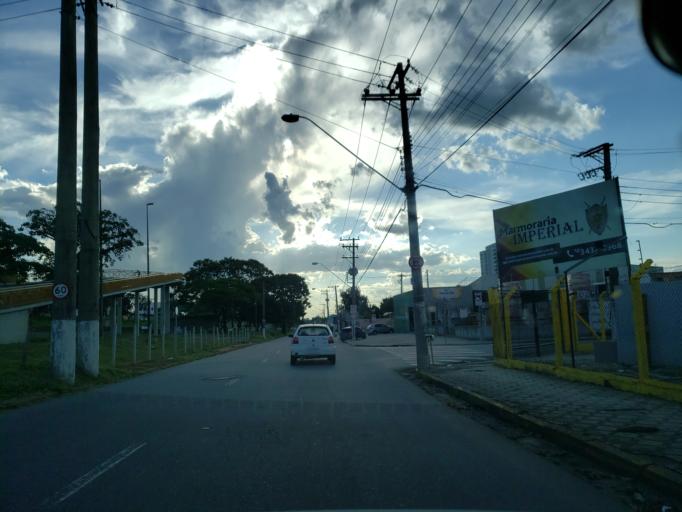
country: BR
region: Sao Paulo
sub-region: Taubate
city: Taubate
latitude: -23.0426
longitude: -45.5767
